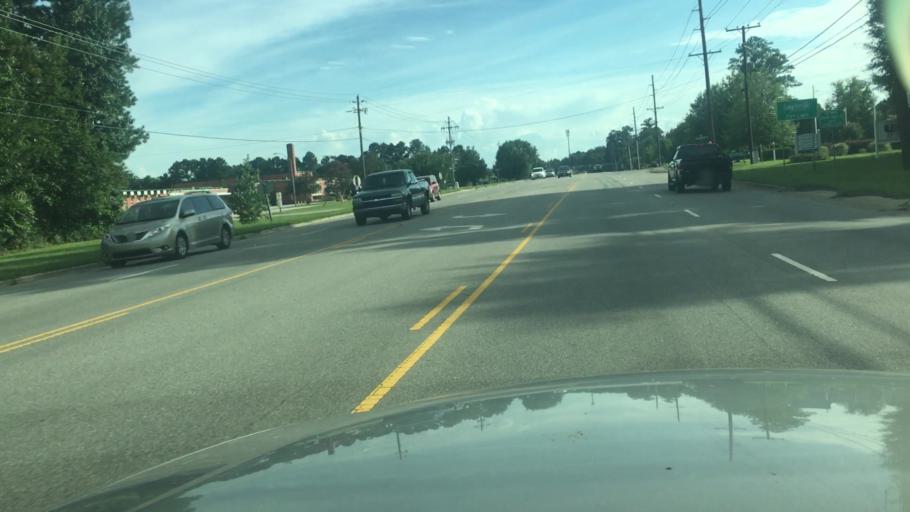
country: US
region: North Carolina
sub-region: Cumberland County
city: Eastover
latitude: 35.1644
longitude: -78.8650
